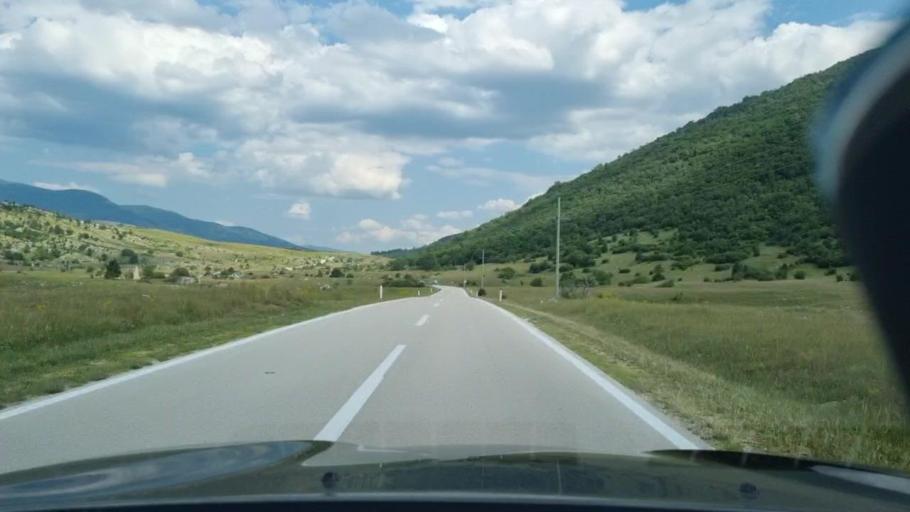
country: BA
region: Federation of Bosnia and Herzegovina
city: Bosansko Grahovo
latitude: 44.1329
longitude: 16.4779
